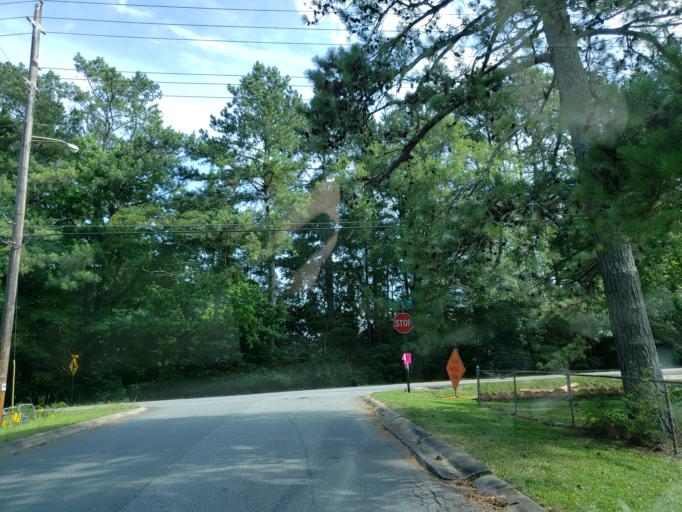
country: US
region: Georgia
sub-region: Cobb County
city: Austell
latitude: 33.8696
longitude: -84.6187
